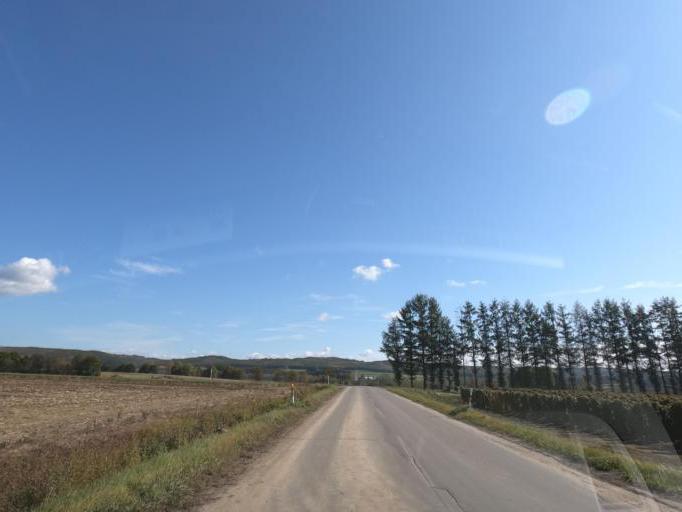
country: JP
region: Hokkaido
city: Otofuke
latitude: 43.0603
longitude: 143.2691
